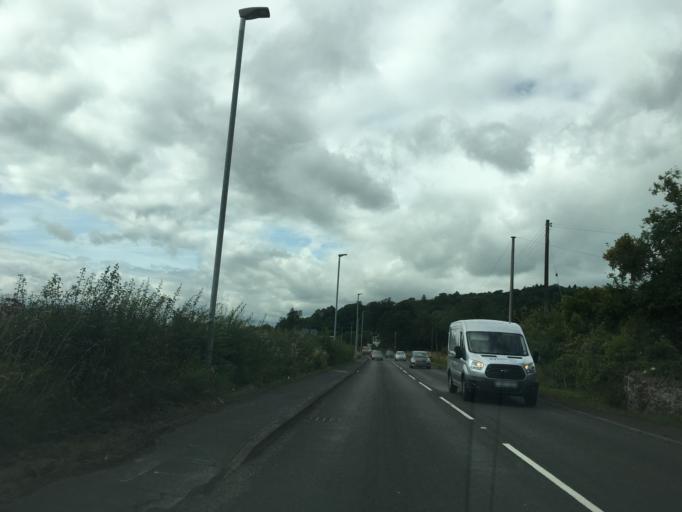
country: GB
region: Scotland
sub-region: Stirling
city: Stirling
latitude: 56.1336
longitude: -3.9028
